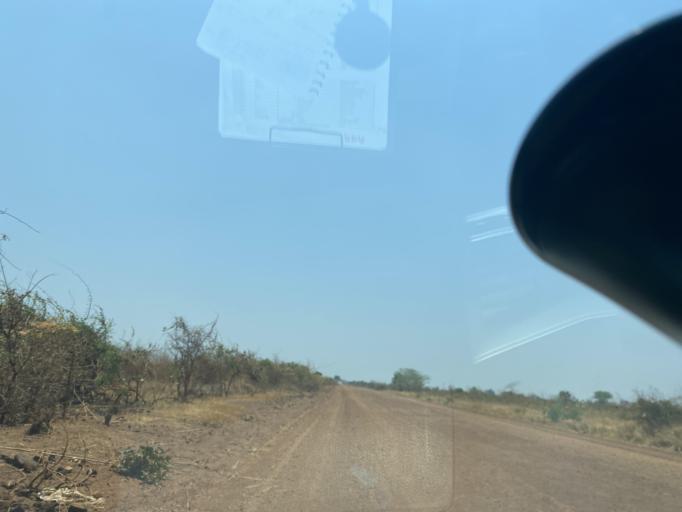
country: ZM
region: Southern
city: Nakambala
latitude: -15.4680
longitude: 27.9055
